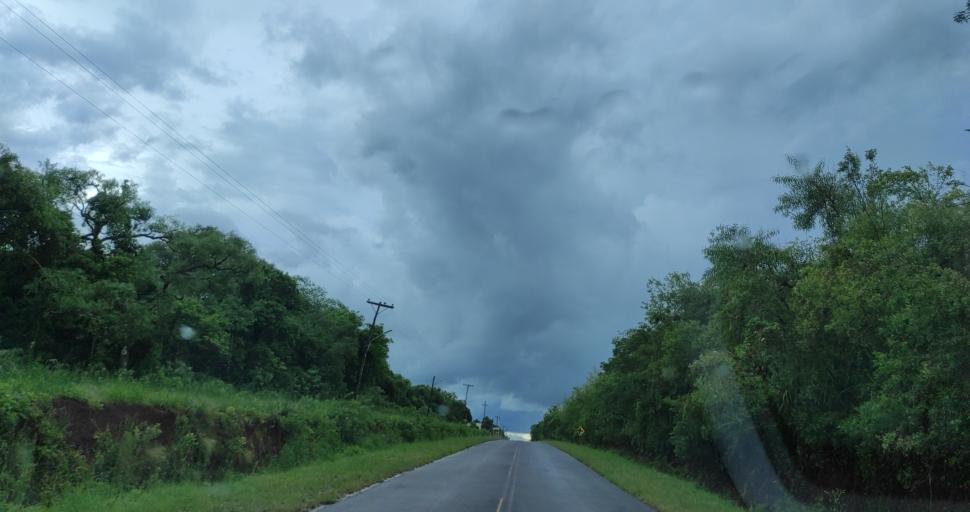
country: AR
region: Misiones
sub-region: Departamento de Apostoles
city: San Jose
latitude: -27.7719
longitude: -55.7647
